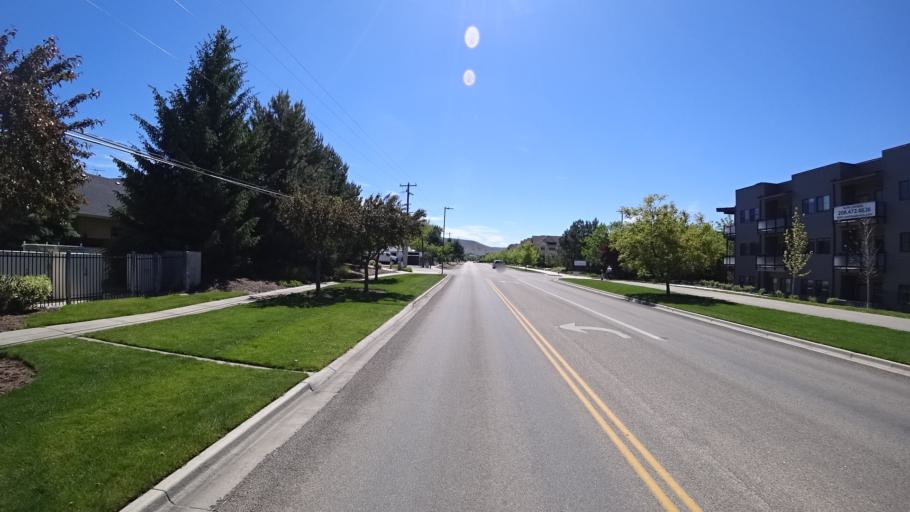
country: US
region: Idaho
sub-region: Ada County
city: Boise
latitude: 43.5682
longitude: -116.1191
